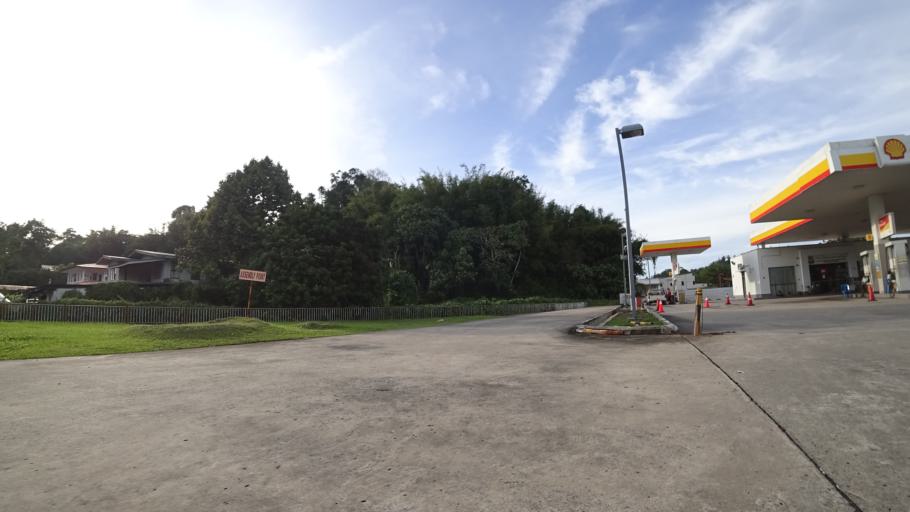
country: BN
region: Brunei and Muara
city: Bandar Seri Begawan
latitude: 4.8810
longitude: 114.8318
